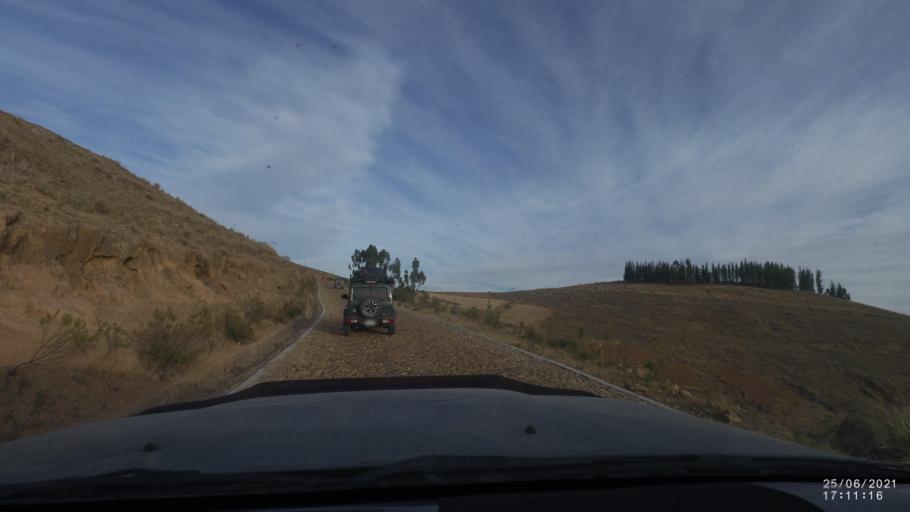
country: BO
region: Cochabamba
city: Arani
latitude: -17.8450
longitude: -65.7044
